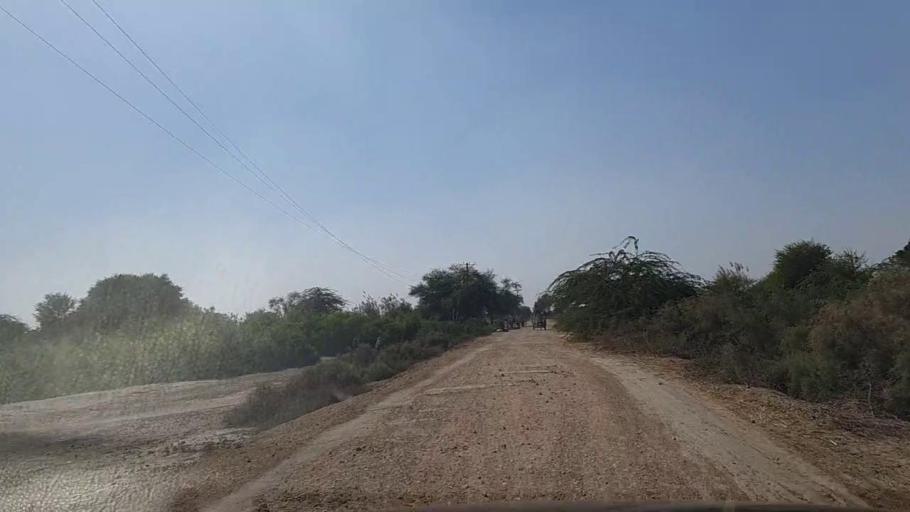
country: PK
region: Sindh
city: Daro Mehar
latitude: 24.8330
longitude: 68.1748
